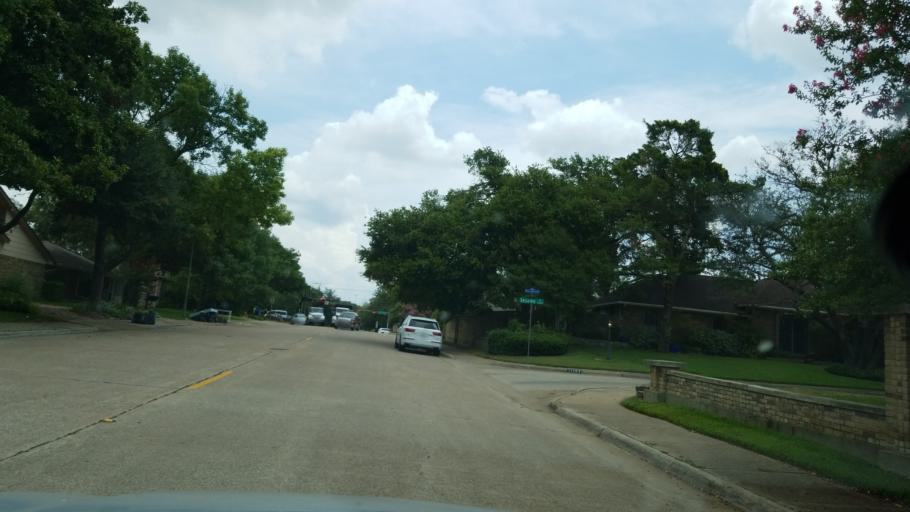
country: US
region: Texas
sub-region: Dallas County
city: Richardson
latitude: 32.8925
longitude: -96.7197
